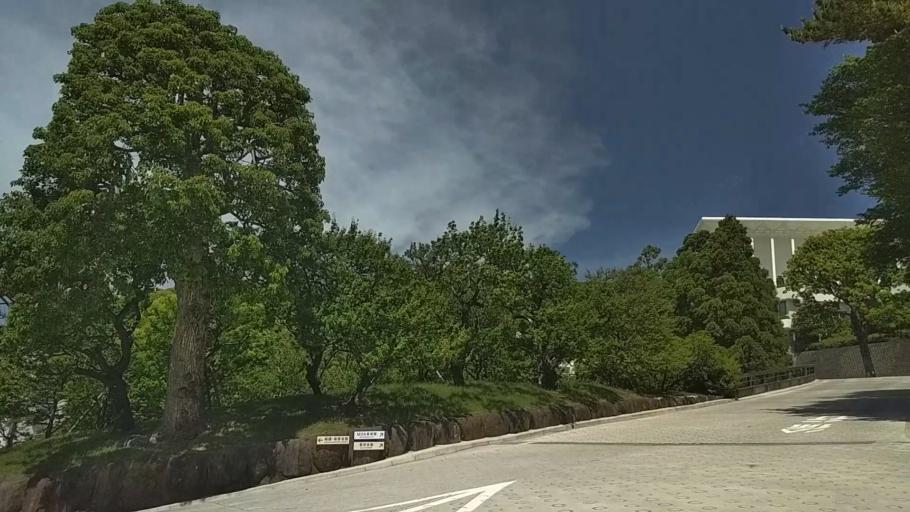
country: JP
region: Shizuoka
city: Atami
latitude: 35.1080
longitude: 139.0793
